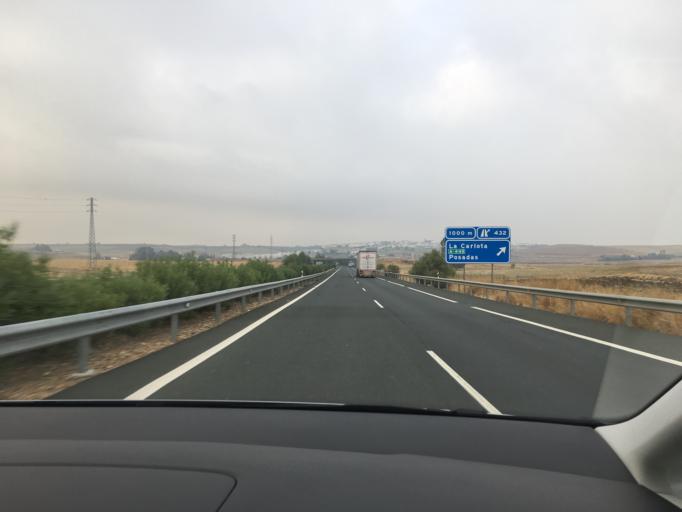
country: ES
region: Andalusia
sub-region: Province of Cordoba
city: La Carlota
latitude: 37.6896
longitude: -4.9223
